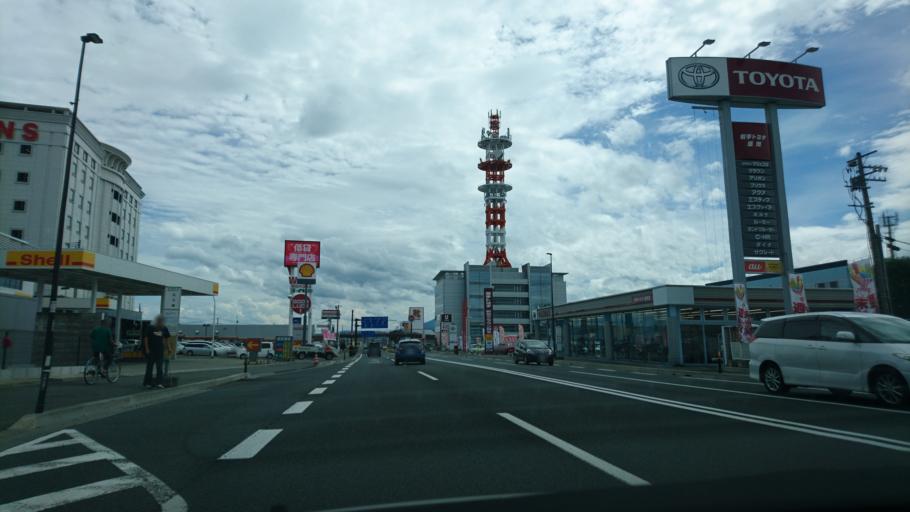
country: JP
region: Iwate
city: Morioka-shi
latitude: 39.7312
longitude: 141.1234
